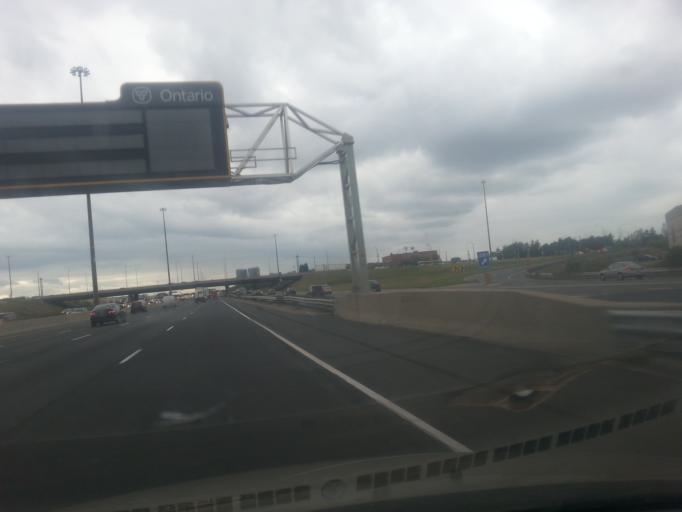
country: CA
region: Ontario
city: Scarborough
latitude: 43.7820
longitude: -79.2512
